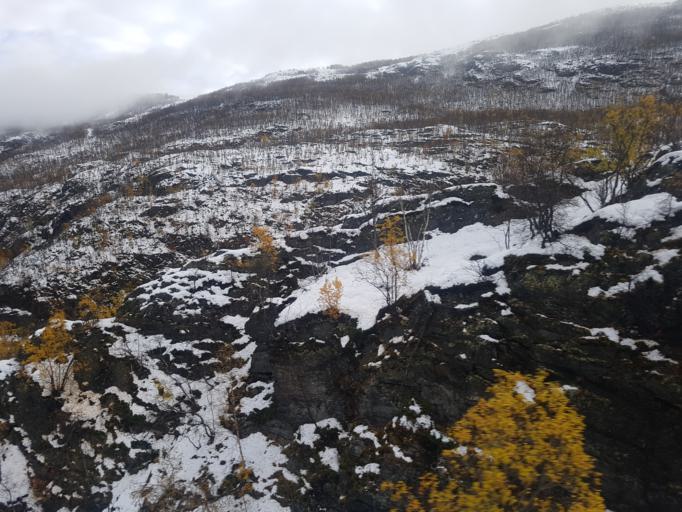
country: NO
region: Sor-Trondelag
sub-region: Oppdal
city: Oppdal
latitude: 62.3458
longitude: 9.6259
